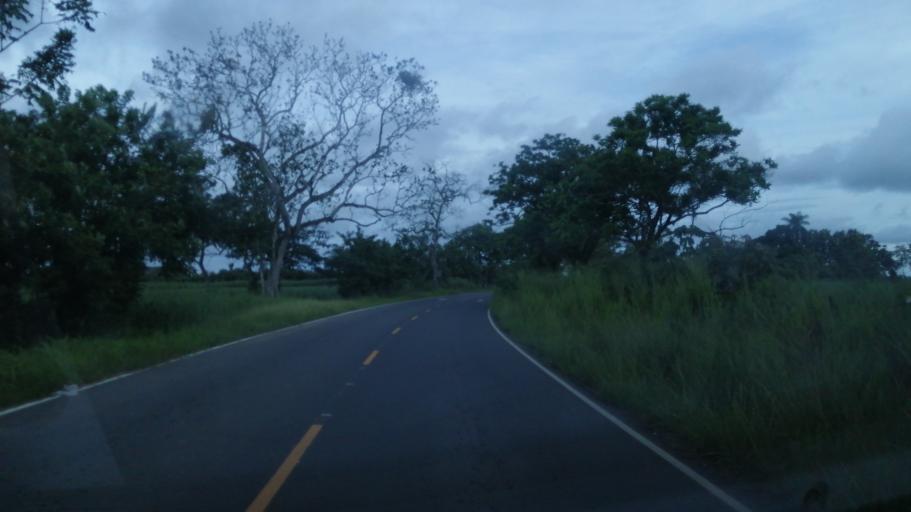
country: PA
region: Chiriqui
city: Alanje
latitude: 8.4078
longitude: -82.5138
